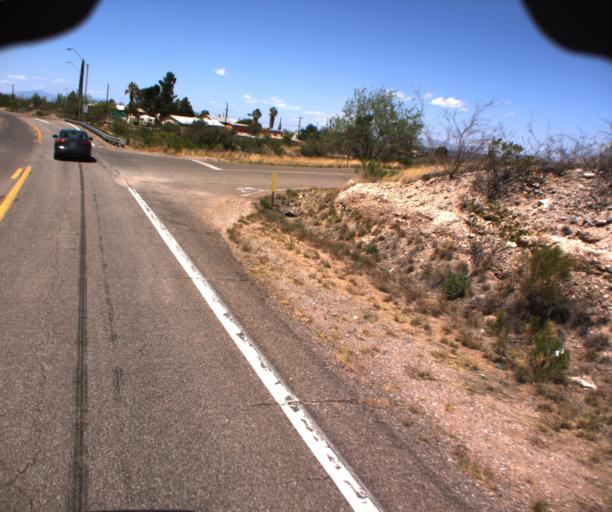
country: US
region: Arizona
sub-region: Cochise County
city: Tombstone
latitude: 31.7088
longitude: -110.0554
